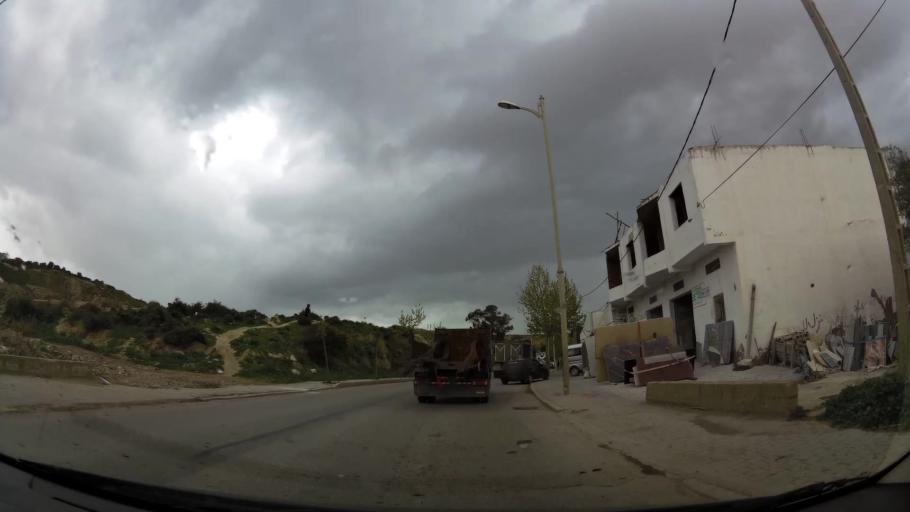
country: MA
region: Tanger-Tetouan
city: Tetouan
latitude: 35.5554
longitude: -5.4017
